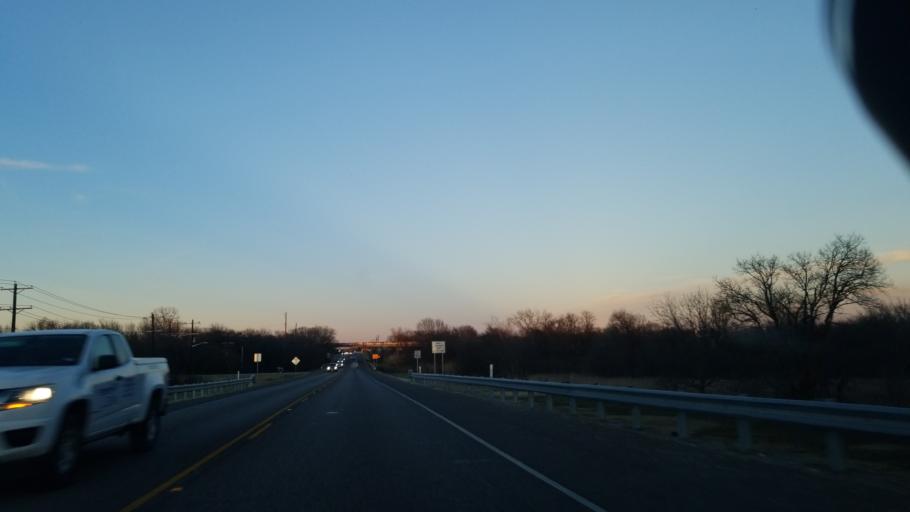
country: US
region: Texas
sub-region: Denton County
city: Denton
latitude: 33.1685
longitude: -97.1521
